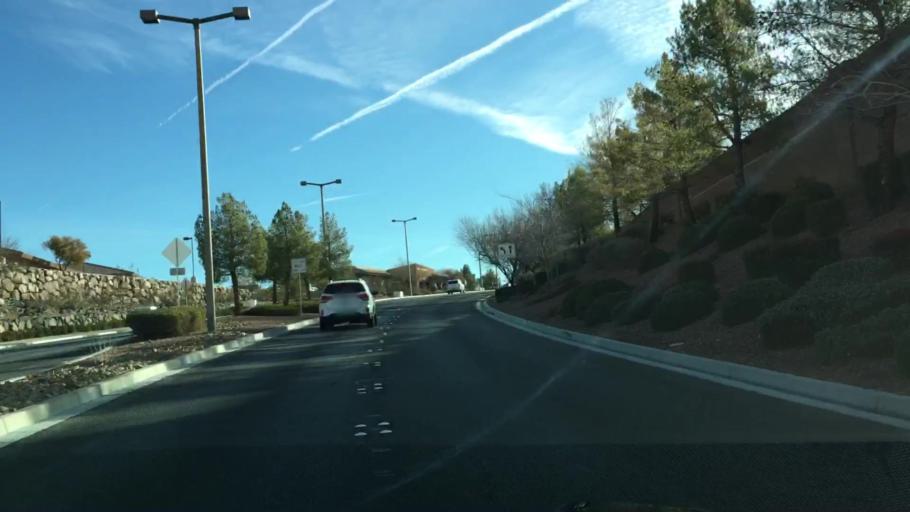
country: US
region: Nevada
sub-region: Clark County
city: Whitney
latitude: 35.9693
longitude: -115.1036
